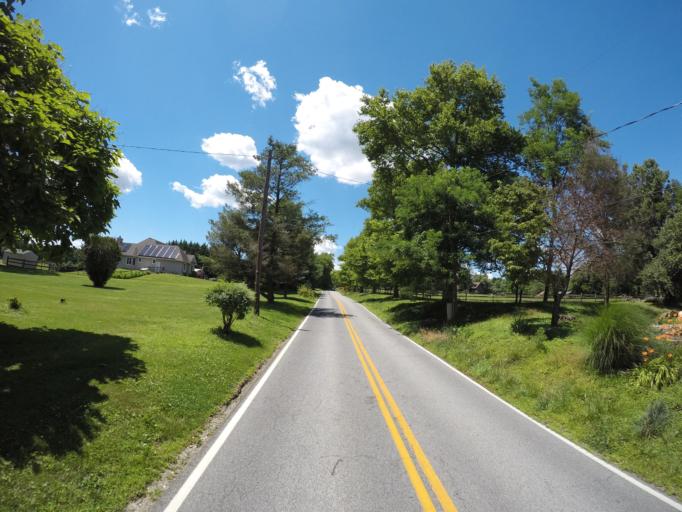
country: US
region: Delaware
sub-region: New Castle County
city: Middletown
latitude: 39.4657
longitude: -75.7768
